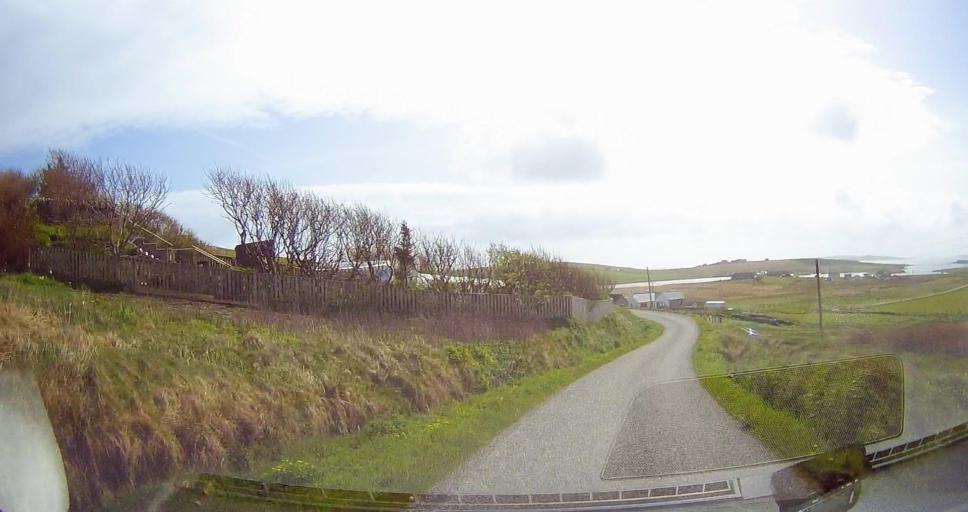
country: GB
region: Scotland
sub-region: Shetland Islands
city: Sandwick
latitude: 60.0488
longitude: -1.2178
